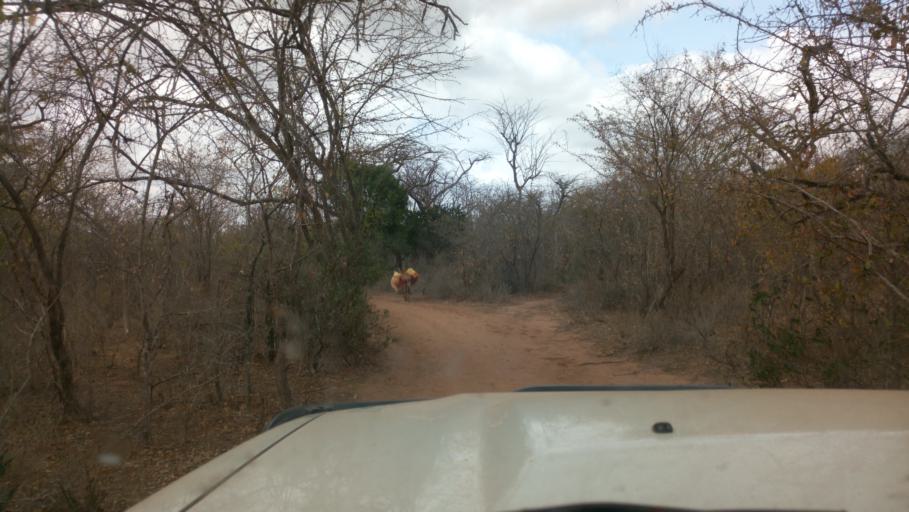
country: KE
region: Kitui
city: Kitui
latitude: -1.8449
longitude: 38.3567
